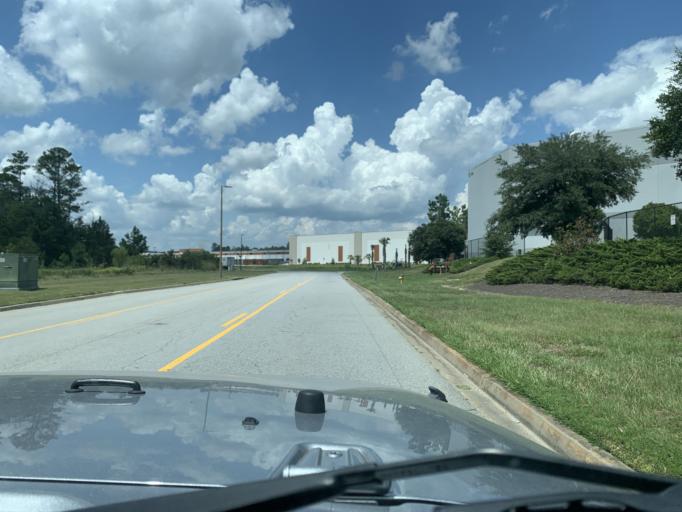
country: US
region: Georgia
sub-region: Chatham County
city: Pooler
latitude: 32.1059
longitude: -81.2734
